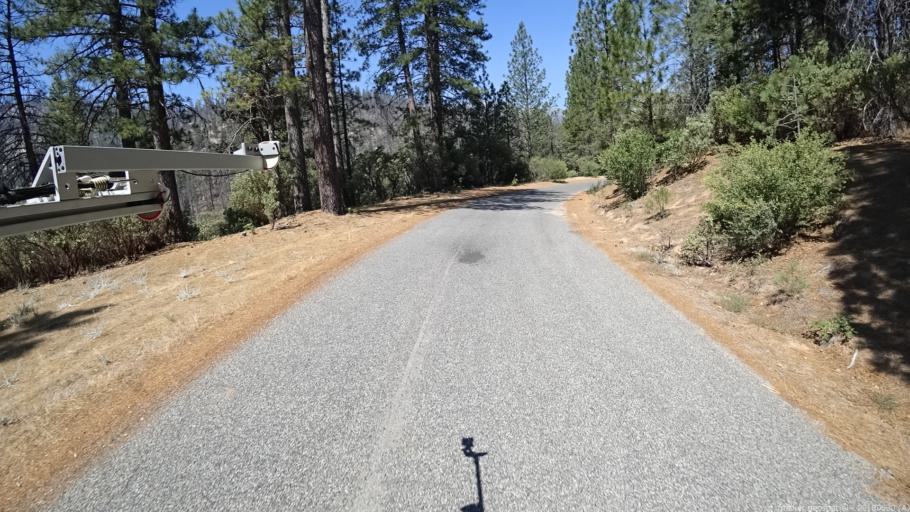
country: US
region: California
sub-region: Madera County
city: Oakhurst
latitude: 37.3589
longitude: -119.3463
